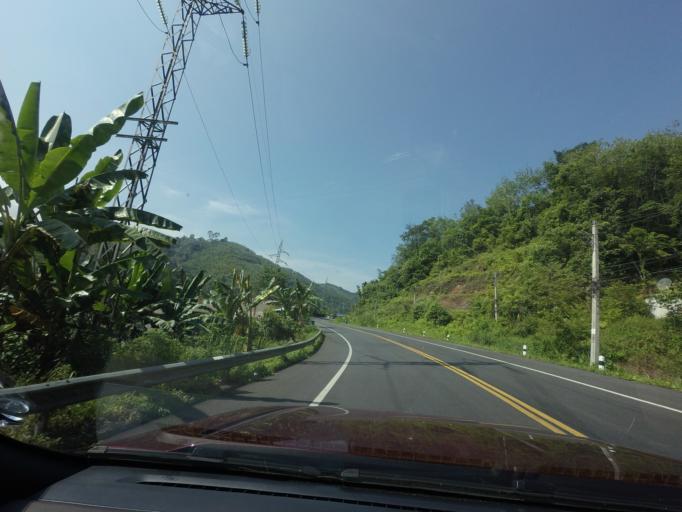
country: TH
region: Yala
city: Than To
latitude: 5.9758
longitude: 101.2008
